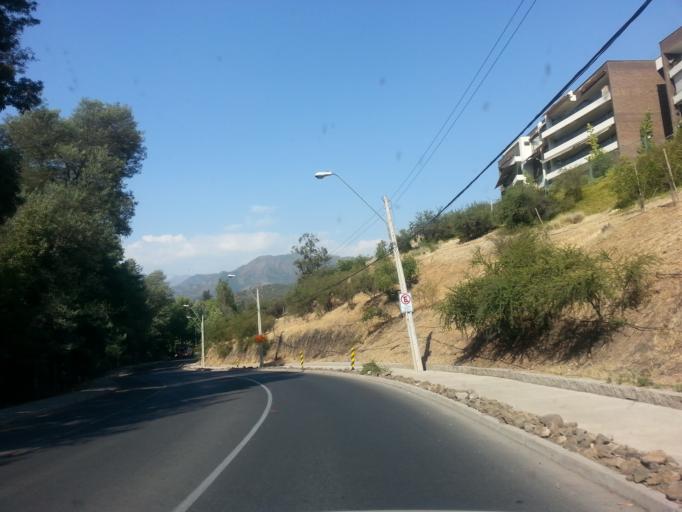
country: CL
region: Santiago Metropolitan
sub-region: Provincia de Santiago
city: Villa Presidente Frei, Nunoa, Santiago, Chile
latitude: -33.3802
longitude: -70.5094
